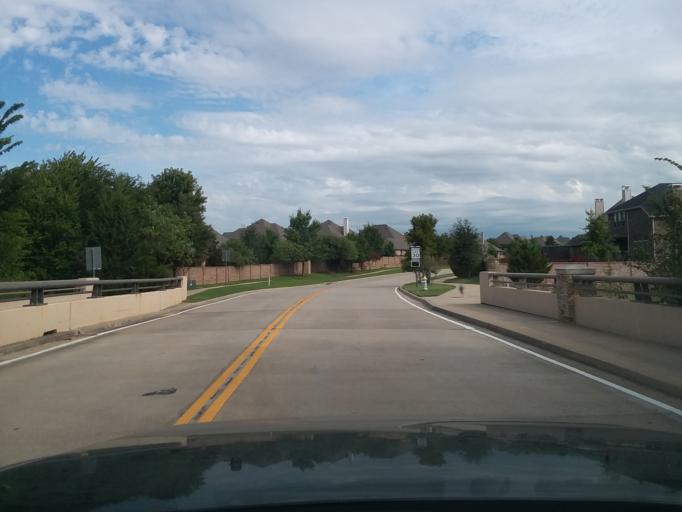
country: US
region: Texas
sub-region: Denton County
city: Copper Canyon
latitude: 33.1101
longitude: -97.1226
